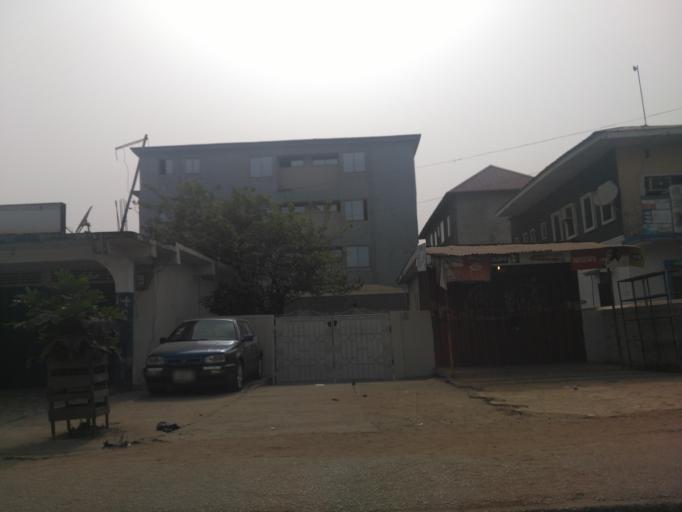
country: GH
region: Ashanti
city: Kumasi
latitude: 6.7050
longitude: -1.6352
